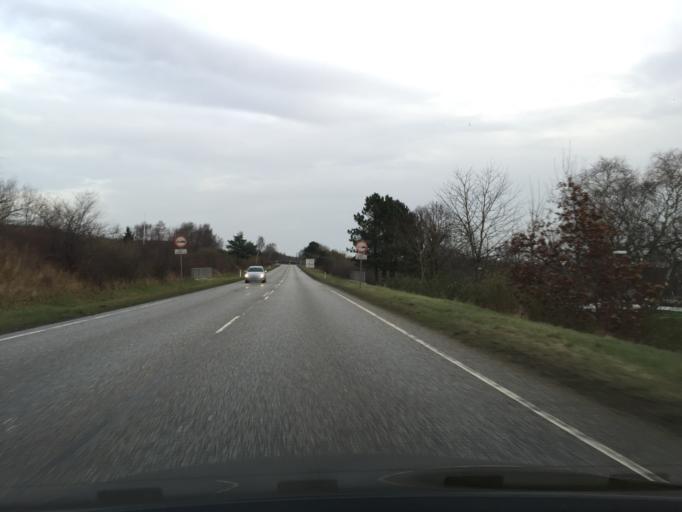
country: DK
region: Central Jutland
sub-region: Viborg Kommune
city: Bjerringbro
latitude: 56.3734
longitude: 9.6319
